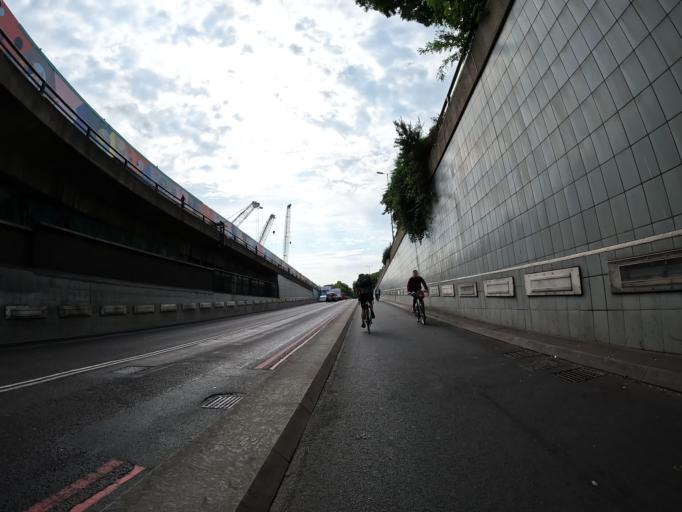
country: GB
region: England
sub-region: Greater London
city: Islington
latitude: 51.5352
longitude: -0.0863
